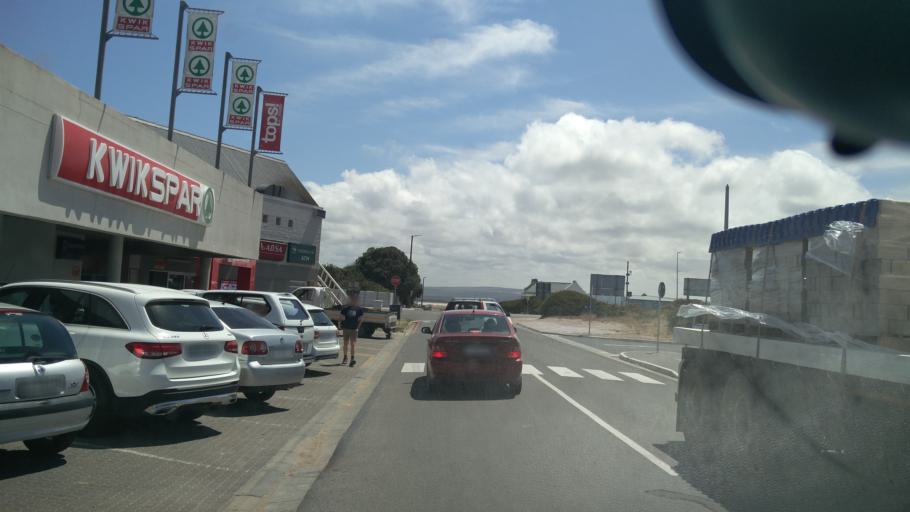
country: ZA
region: Western Cape
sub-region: City of Cape Town
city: Atlantis
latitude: -33.3451
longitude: 18.1617
